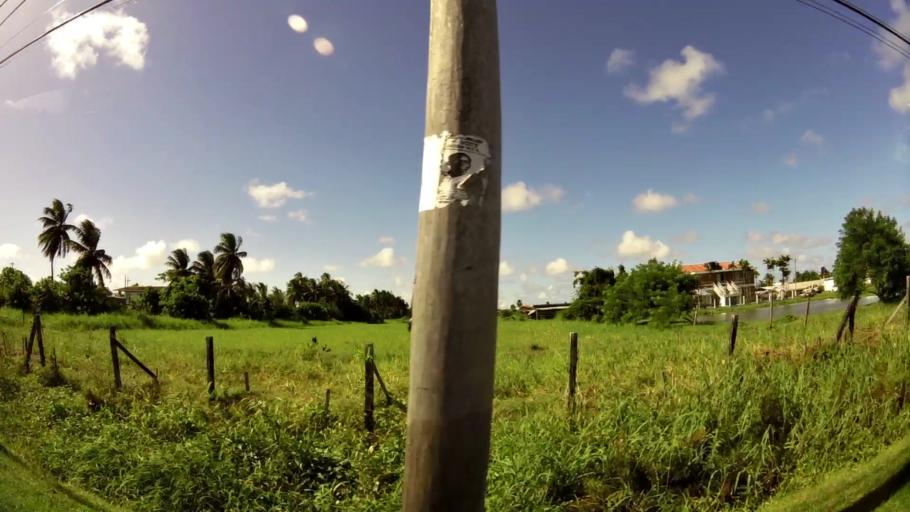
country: GY
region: Demerara-Mahaica
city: Georgetown
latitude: 6.8211
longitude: -58.1261
